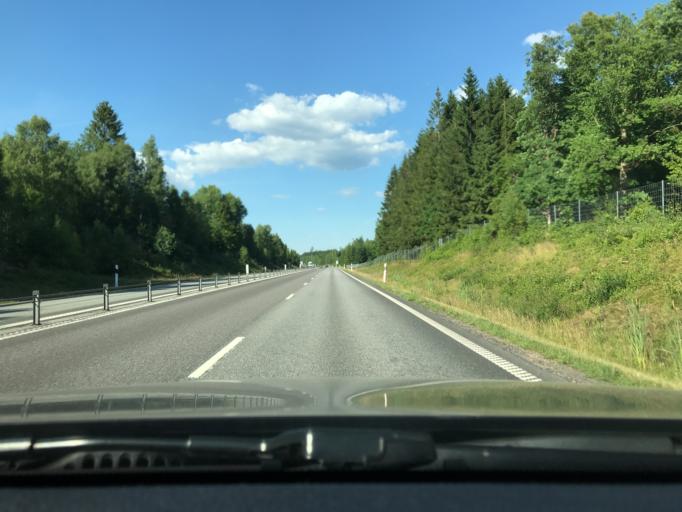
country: SE
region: Kronoberg
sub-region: Almhults Kommun
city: AElmhult
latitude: 56.4545
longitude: 14.0883
